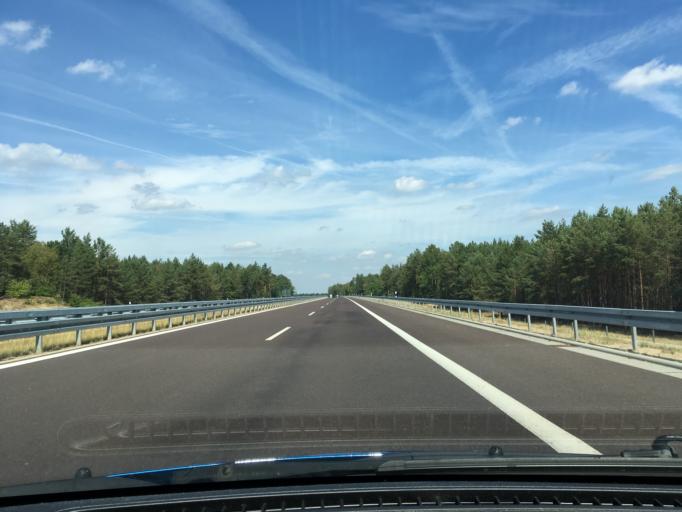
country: DE
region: Mecklenburg-Vorpommern
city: Ludwigslust
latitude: 53.3173
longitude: 11.5281
